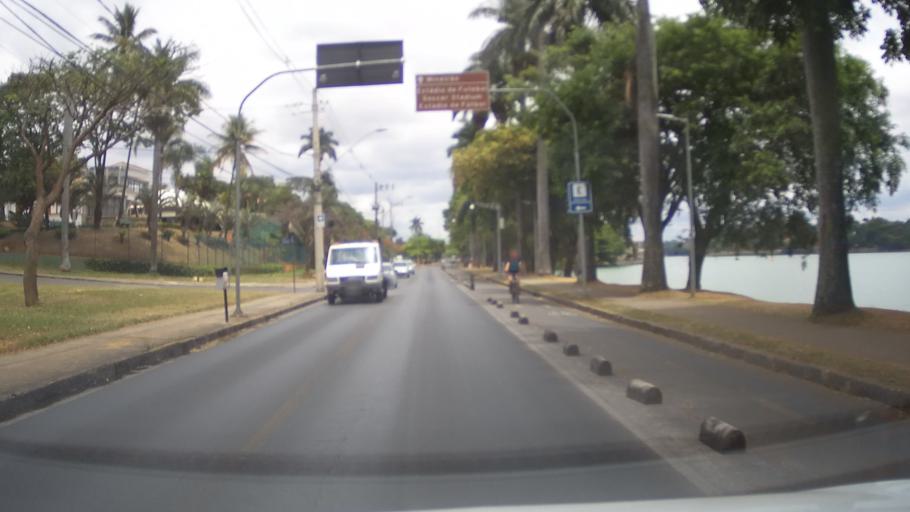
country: BR
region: Minas Gerais
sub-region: Belo Horizonte
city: Belo Horizonte
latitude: -19.8551
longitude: -43.9722
